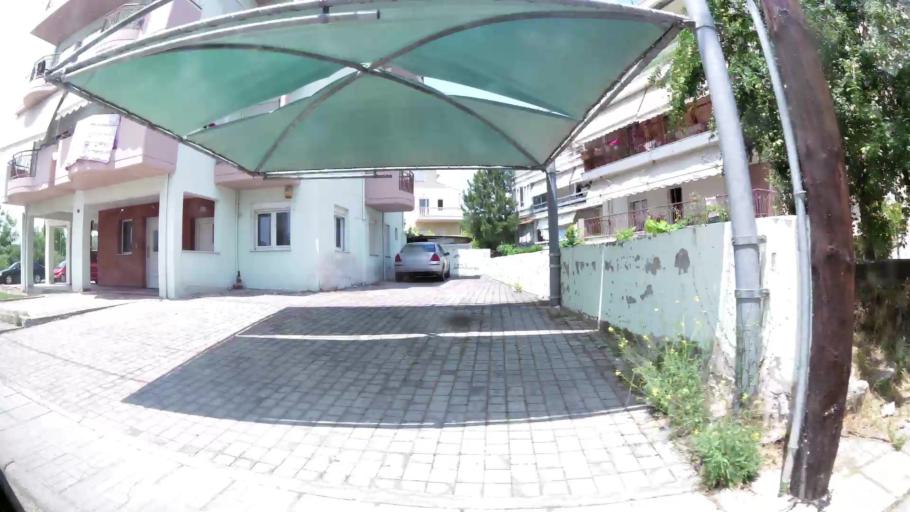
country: GR
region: West Macedonia
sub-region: Nomos Kozanis
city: Kozani
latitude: 40.2883
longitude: 21.7810
